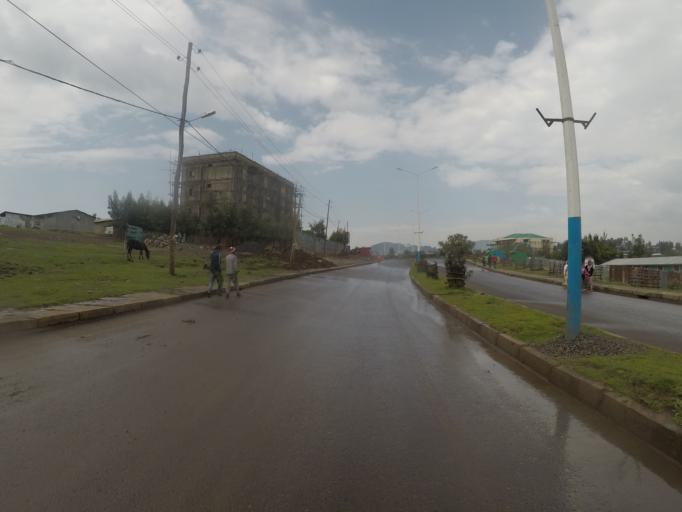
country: ET
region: Amhara
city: Debark'
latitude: 13.1446
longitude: 37.8939
